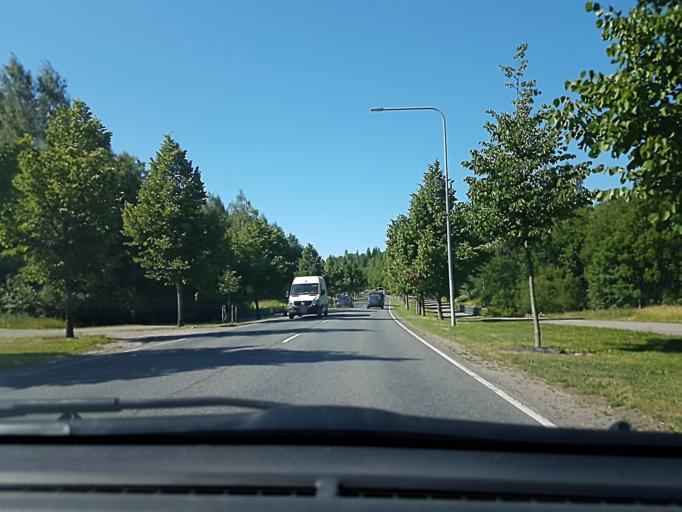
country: FI
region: Uusimaa
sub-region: Helsinki
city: Vantaa
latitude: 60.3426
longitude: 25.0729
